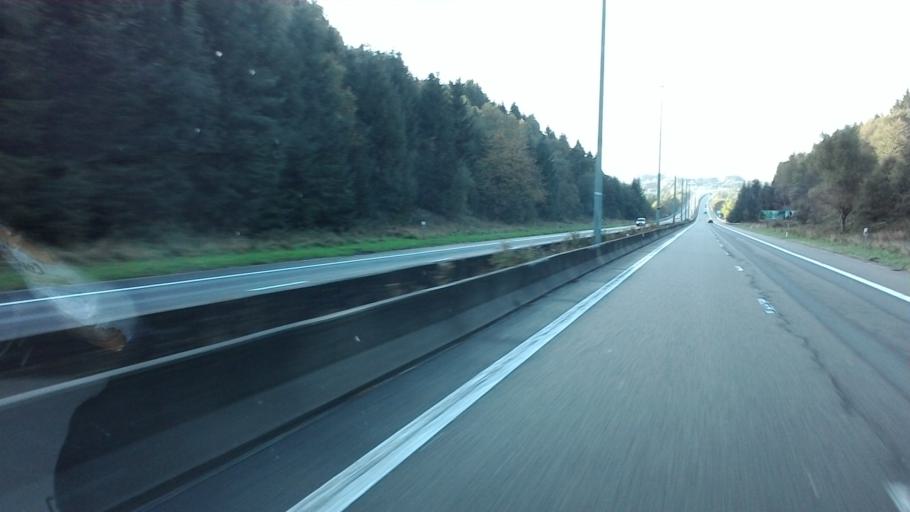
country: BE
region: Wallonia
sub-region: Province du Luxembourg
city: Manhay
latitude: 50.3478
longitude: 5.6847
